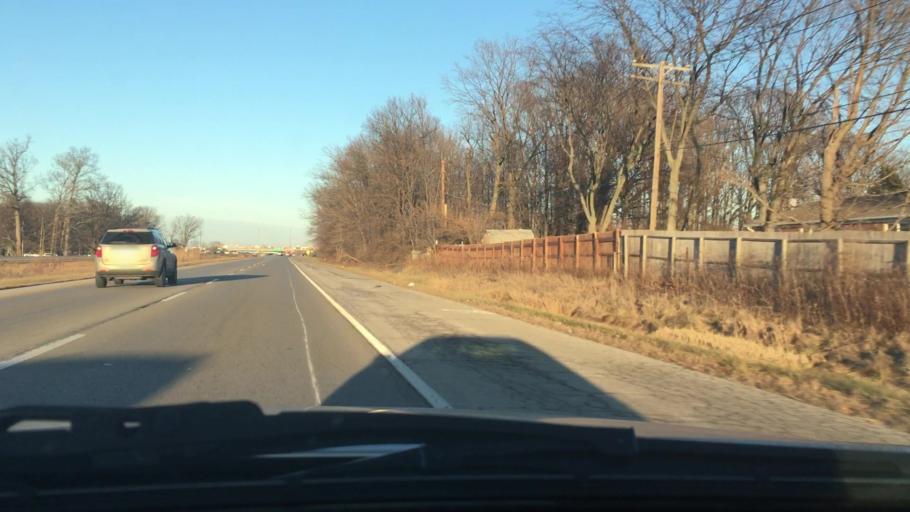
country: US
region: Indiana
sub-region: Marion County
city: Lawrence
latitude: 39.8866
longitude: -86.0632
